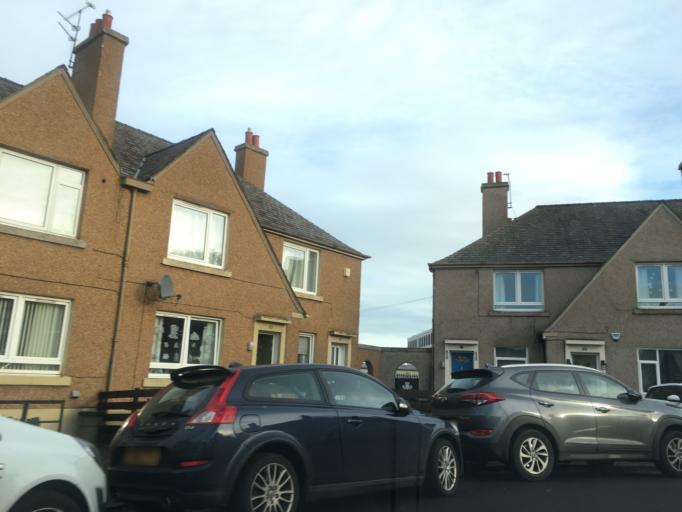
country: GB
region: Scotland
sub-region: Edinburgh
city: Colinton
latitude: 55.9337
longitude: -3.2434
